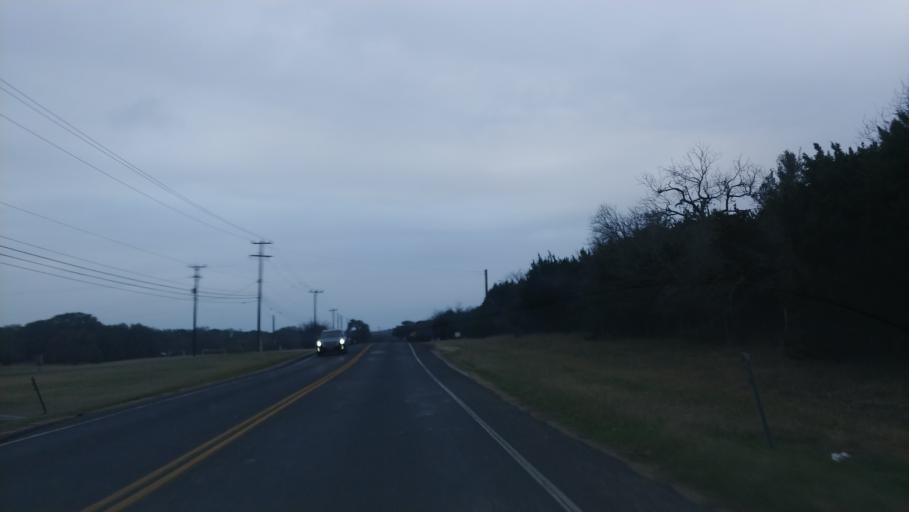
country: US
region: Texas
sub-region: Bexar County
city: Cross Mountain
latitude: 29.6724
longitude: -98.6538
